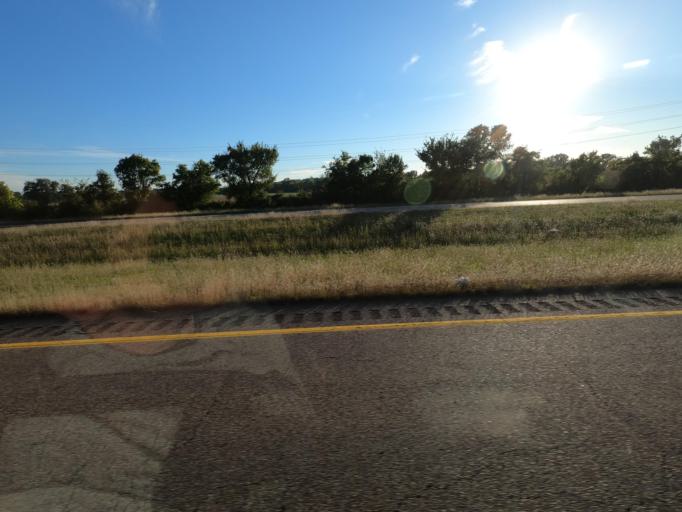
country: US
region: Tennessee
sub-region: Shelby County
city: Millington
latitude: 35.3278
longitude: -89.8878
